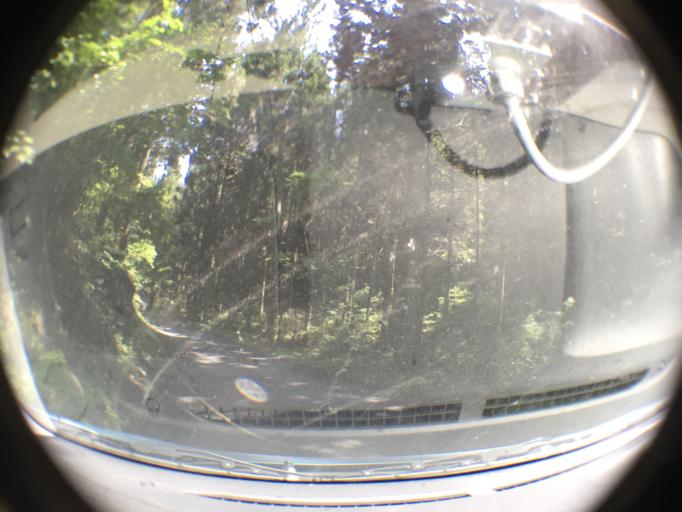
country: JP
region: Iwate
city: Ichinoseki
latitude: 38.7805
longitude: 141.4192
